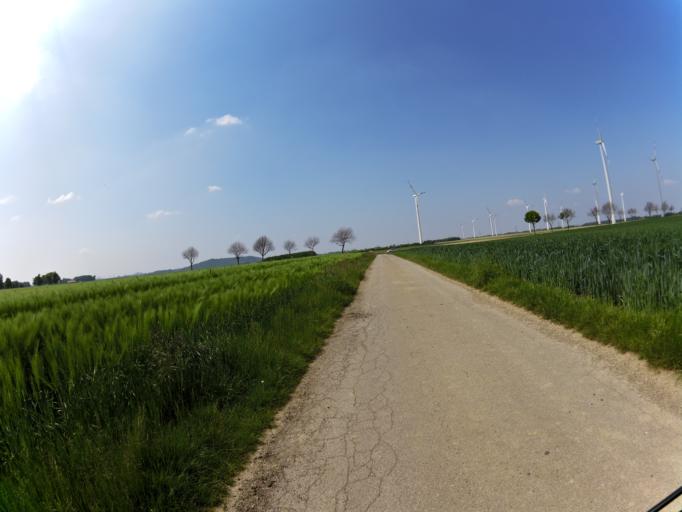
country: DE
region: North Rhine-Westphalia
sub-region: Regierungsbezirk Koln
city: Aldenhoven
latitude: 50.9206
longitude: 6.2820
